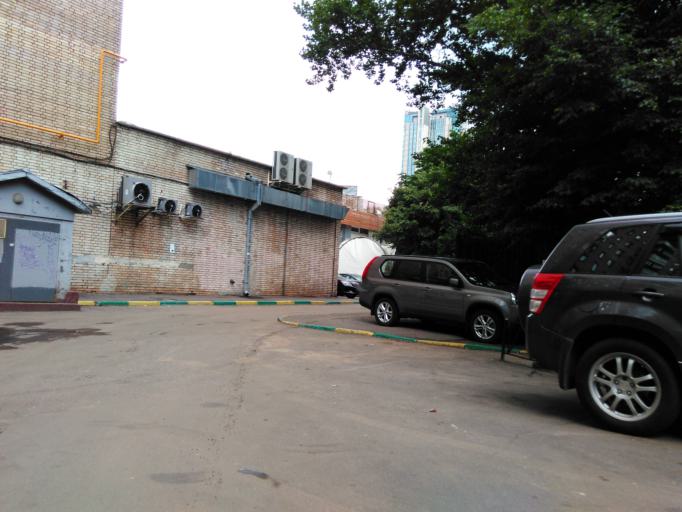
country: RU
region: Moscow
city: Ramenki
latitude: 55.6841
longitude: 37.5215
